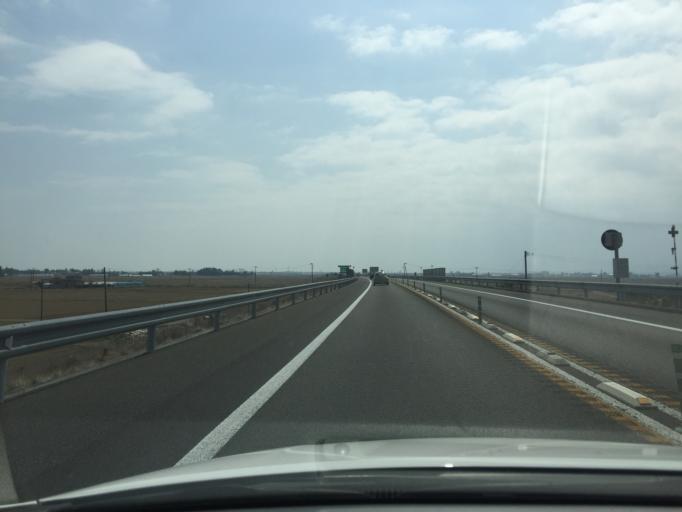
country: JP
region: Miyagi
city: Iwanuma
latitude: 38.0801
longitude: 140.8879
